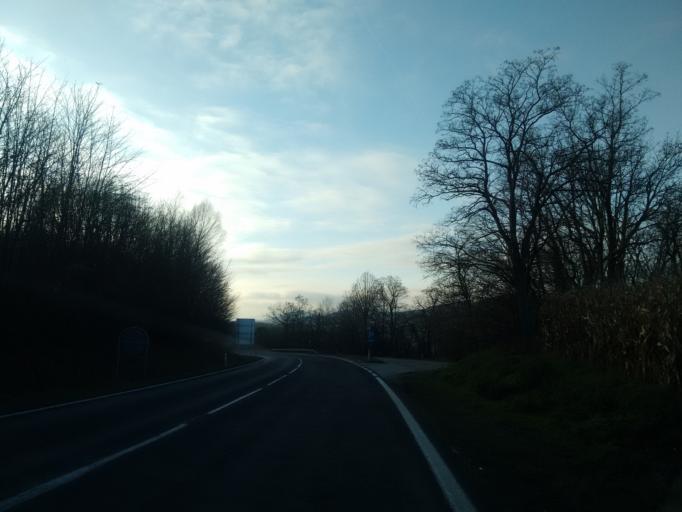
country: AT
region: Lower Austria
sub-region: Politischer Bezirk Melk
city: Emmersdorf an der Donau
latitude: 48.2341
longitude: 15.3442
